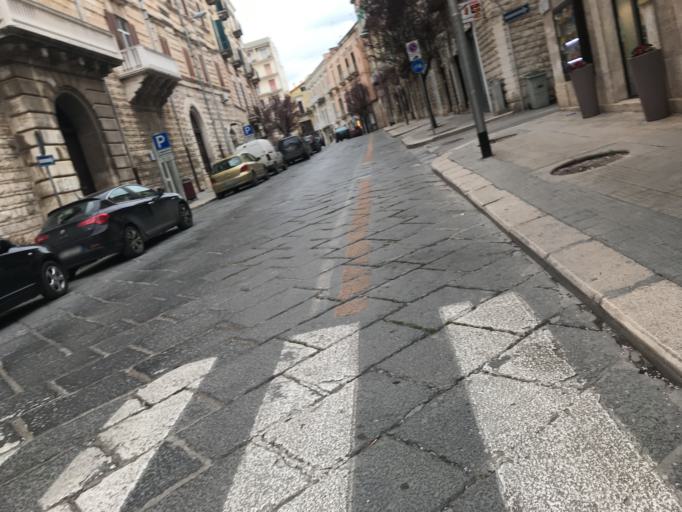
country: IT
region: Apulia
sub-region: Provincia di Bari
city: Corato
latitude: 41.1535
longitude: 16.4094
